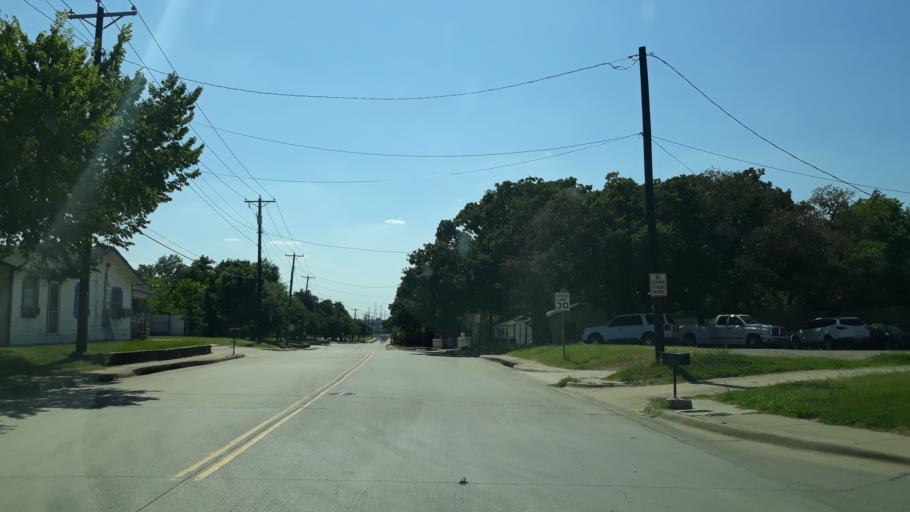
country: US
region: Texas
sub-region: Dallas County
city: Irving
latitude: 32.8173
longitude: -97.0039
